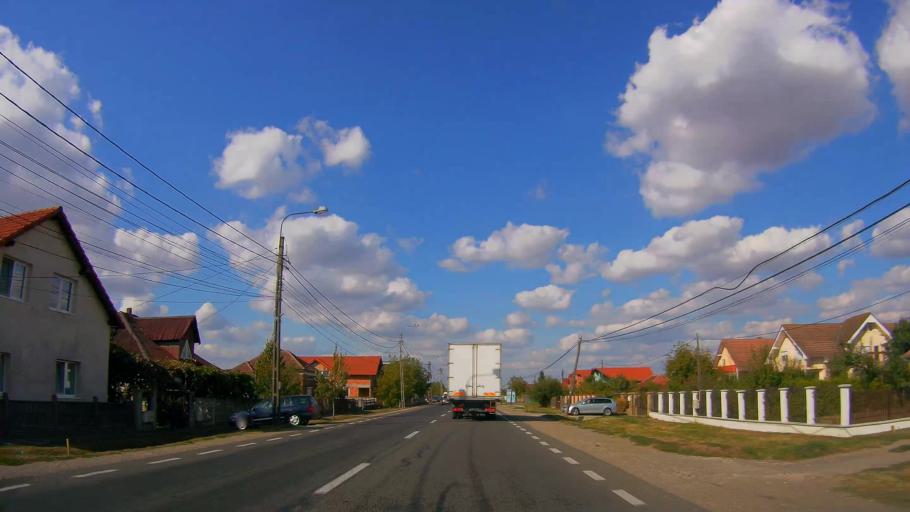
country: RO
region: Satu Mare
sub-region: Oras Ardud
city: Madaras
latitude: 47.7340
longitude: 22.8825
